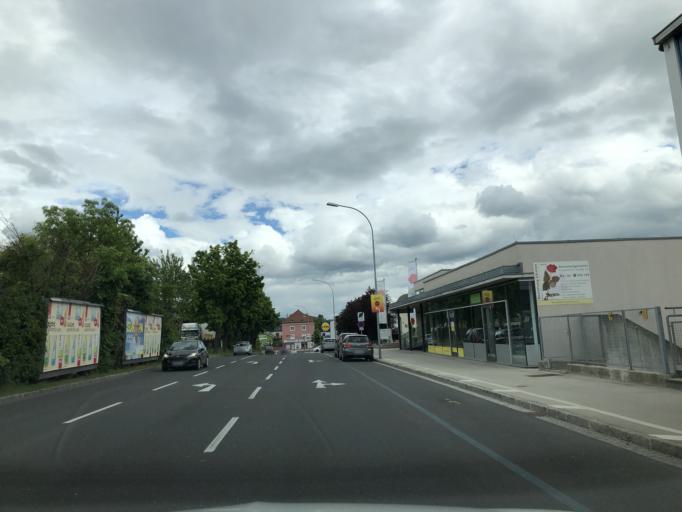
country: AT
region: Carinthia
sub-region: Villach Stadt
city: Villach
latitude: 46.6190
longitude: 13.8582
